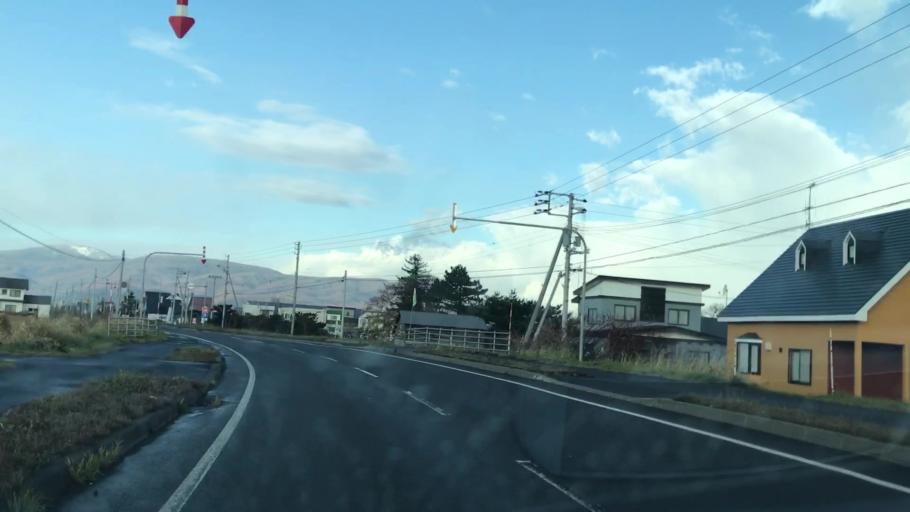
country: JP
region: Hokkaido
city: Yoichi
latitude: 43.1827
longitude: 140.8173
